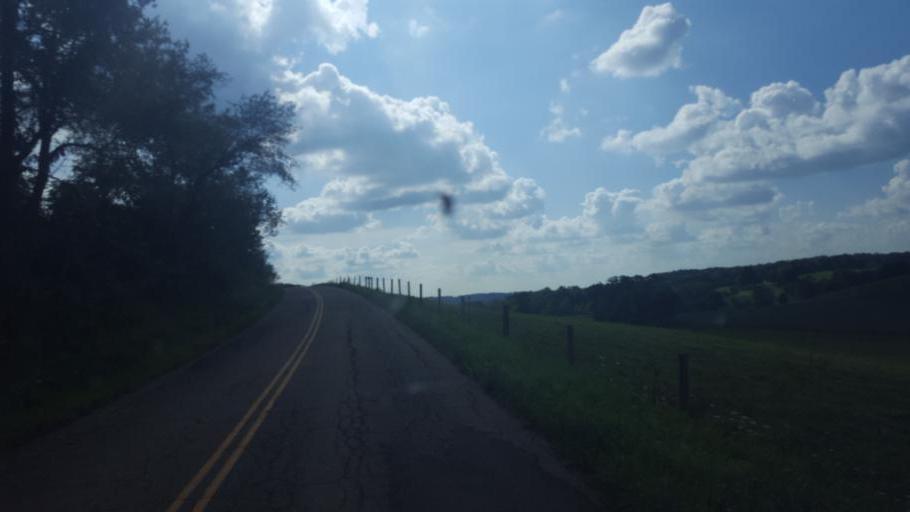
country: US
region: Ohio
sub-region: Knox County
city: Oak Hill
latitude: 40.4040
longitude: -82.2647
